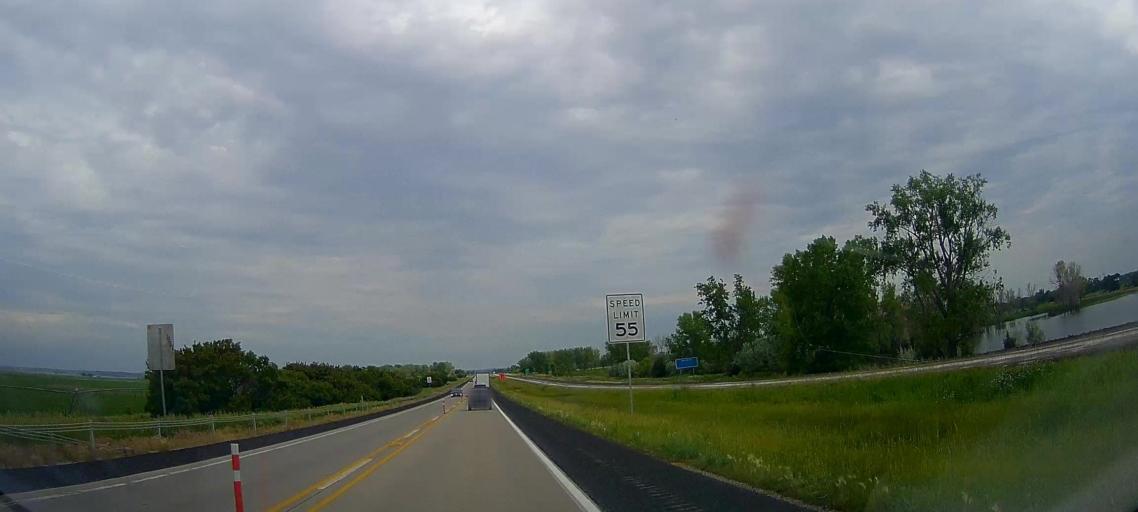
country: US
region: Iowa
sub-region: Harrison County
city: Missouri Valley
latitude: 41.6375
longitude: -96.0101
